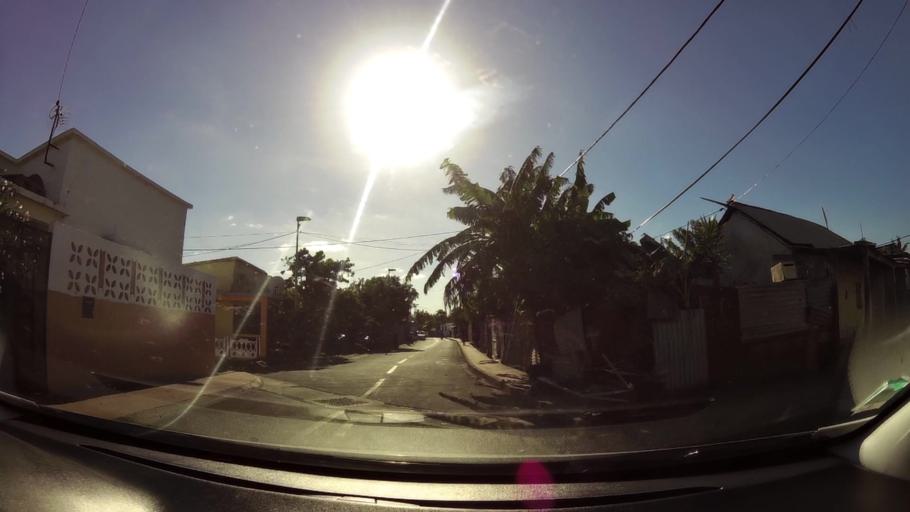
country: YT
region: Pamandzi
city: Pamandzi
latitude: -12.8000
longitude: 45.2762
